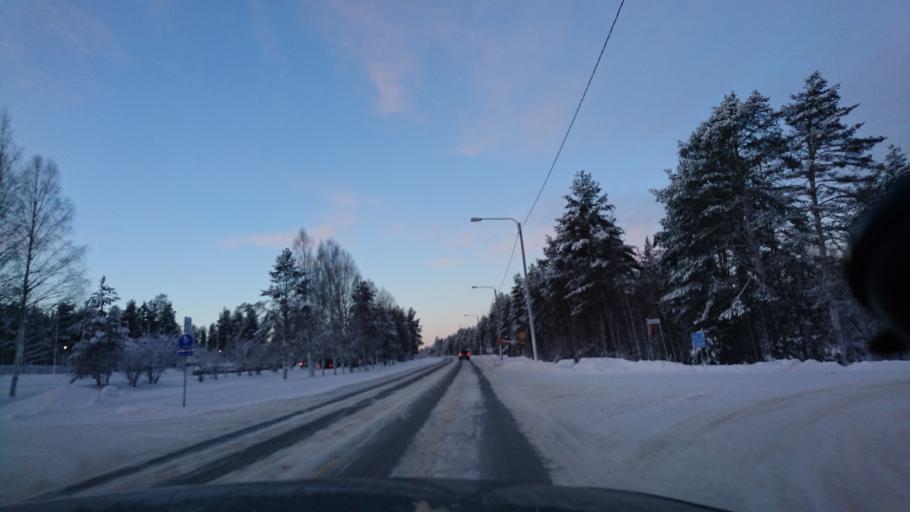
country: FI
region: Lapland
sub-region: Rovaniemi
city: Ranua
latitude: 65.9429
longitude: 26.4727
